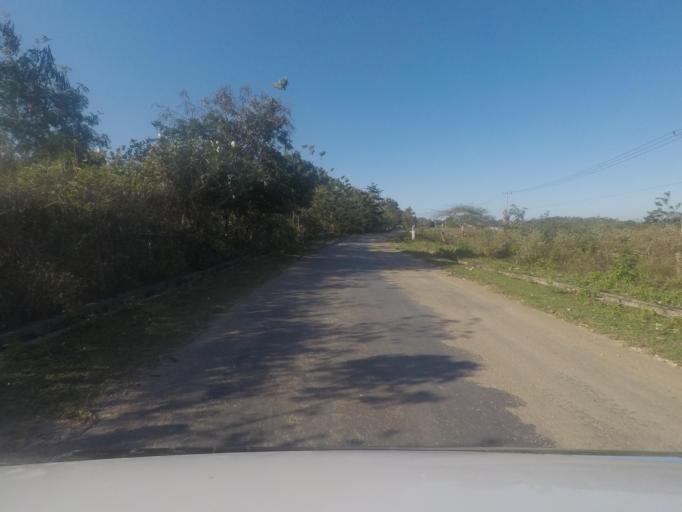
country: TL
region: Lautem
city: Lospalos
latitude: -8.4051
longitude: 127.1755
